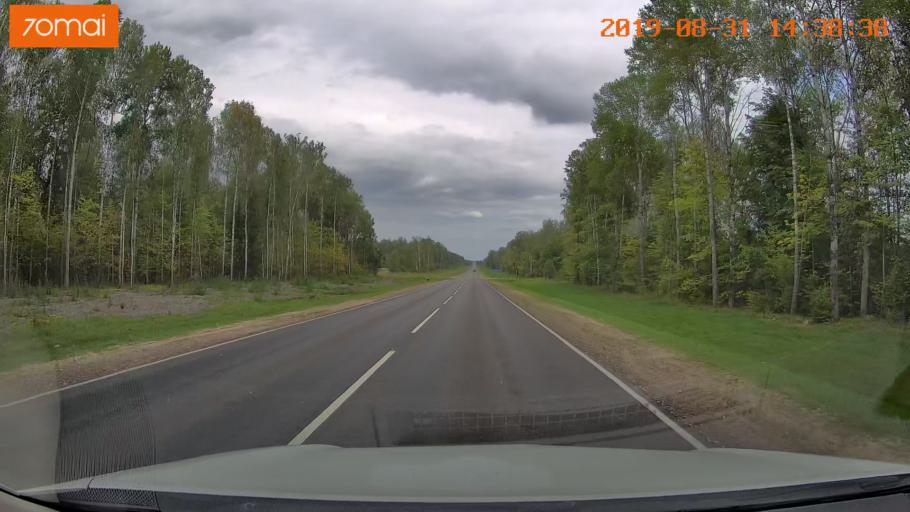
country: RU
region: Smolensk
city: Yekimovichi
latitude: 54.1859
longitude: 33.5332
